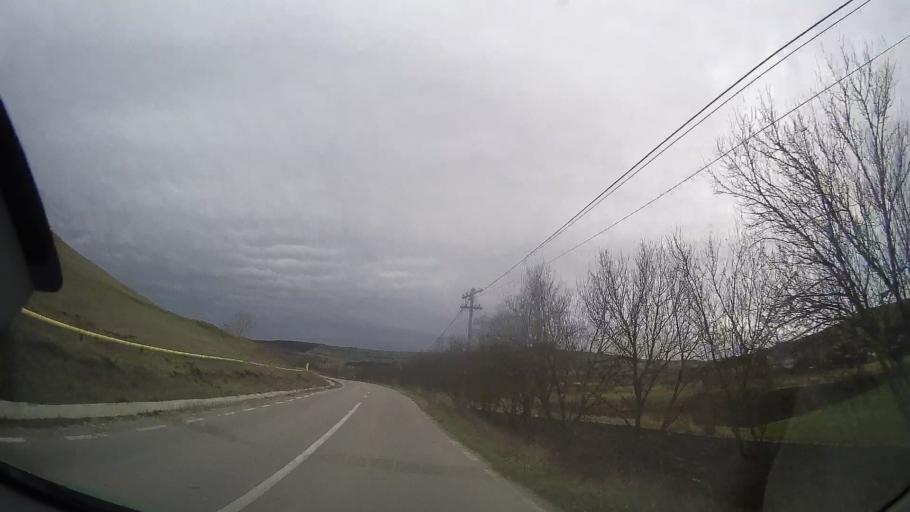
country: RO
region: Cluj
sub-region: Comuna Geaca
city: Geaca
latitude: 46.8457
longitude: 24.1382
